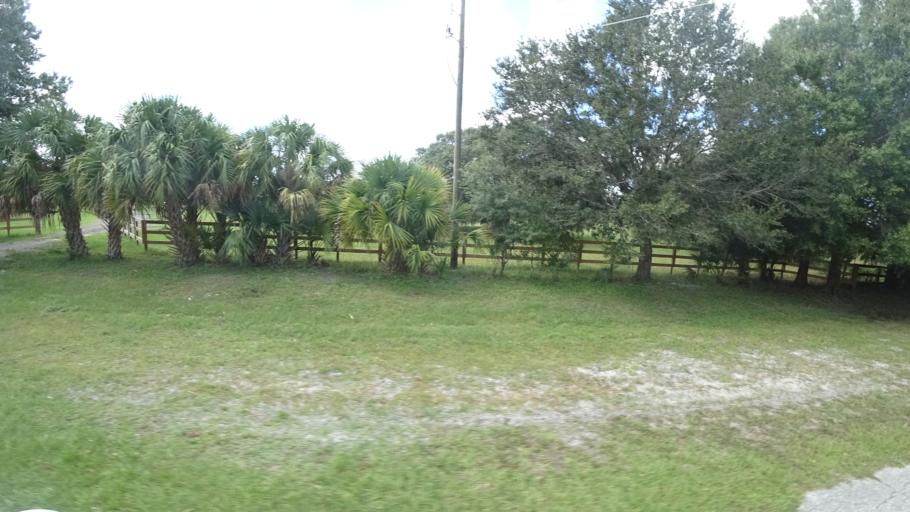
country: US
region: Florida
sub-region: Sarasota County
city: Lake Sarasota
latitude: 27.2834
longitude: -82.2301
